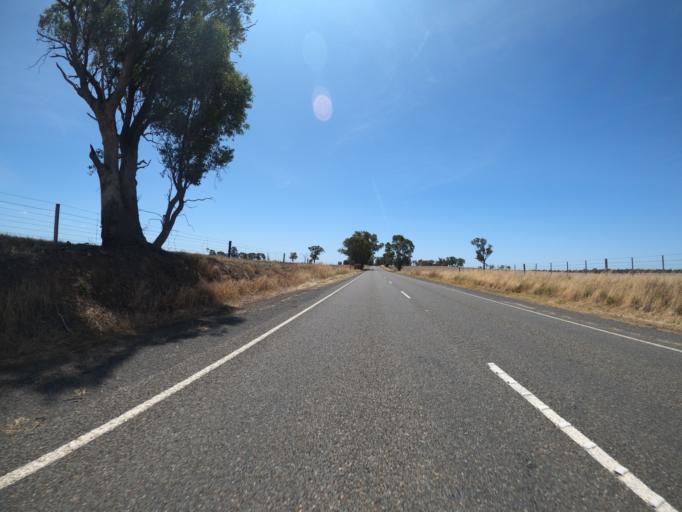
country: AU
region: Victoria
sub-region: Moira
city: Yarrawonga
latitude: -36.0934
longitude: 145.9954
